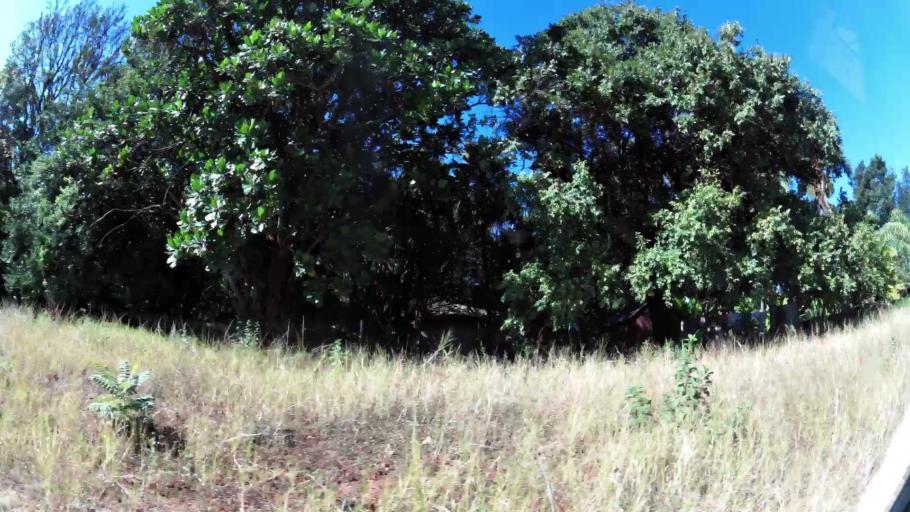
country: ZA
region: Limpopo
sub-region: Mopani District Municipality
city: Tzaneen
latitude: -23.8187
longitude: 30.1555
